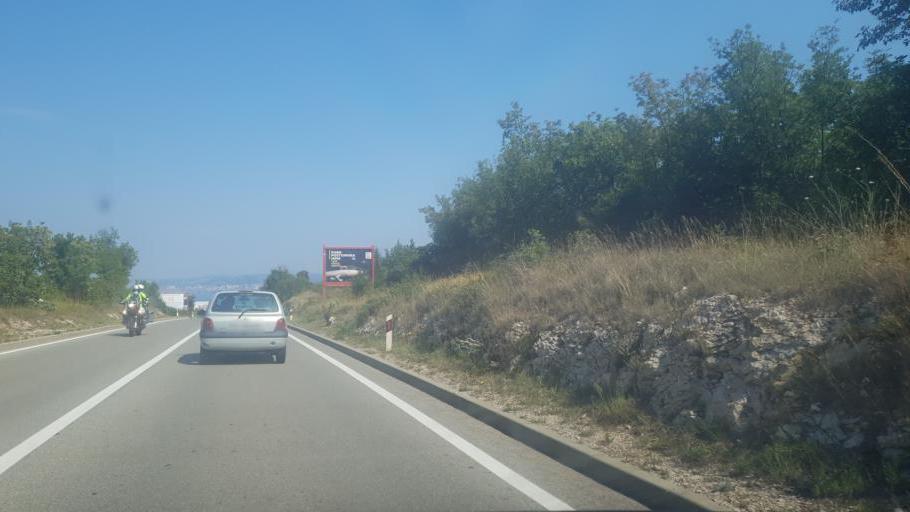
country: HR
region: Primorsko-Goranska
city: Omisalj
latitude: 45.2240
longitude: 14.5599
